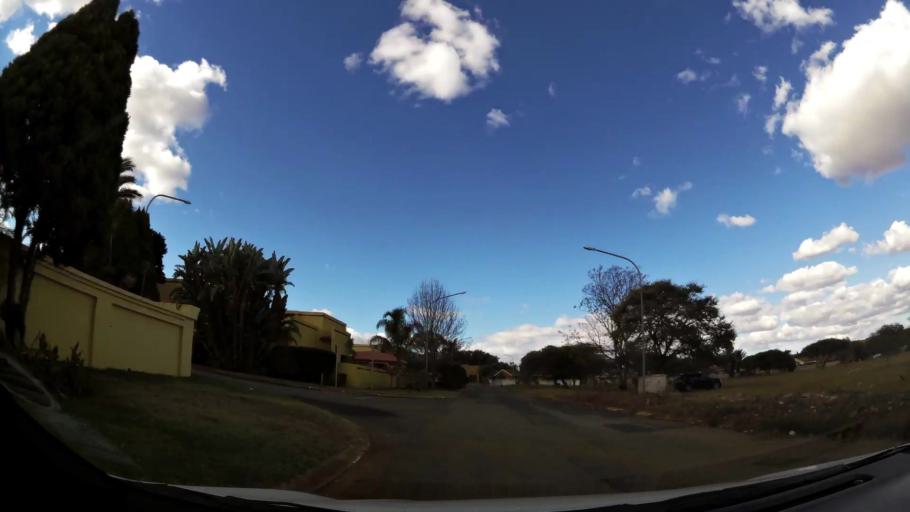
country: ZA
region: Limpopo
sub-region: Capricorn District Municipality
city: Polokwane
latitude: -23.9026
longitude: 29.4961
